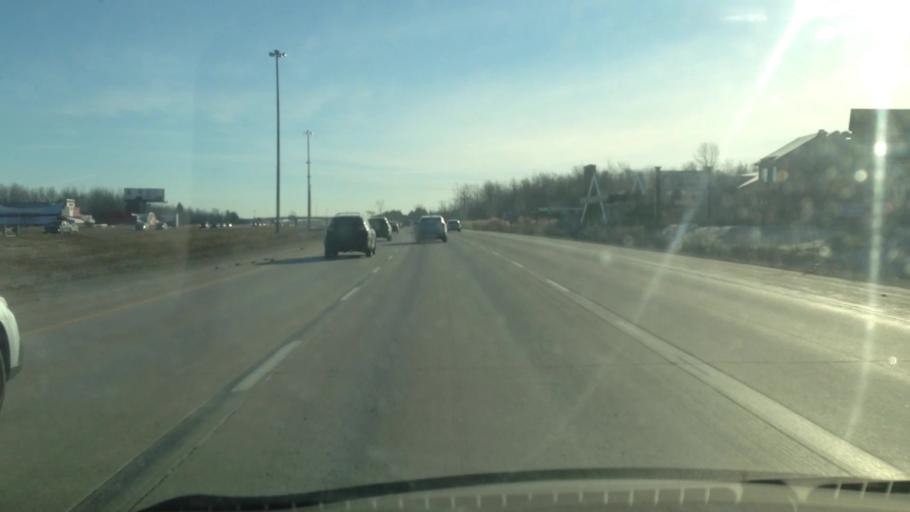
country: CA
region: Quebec
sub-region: Laurentides
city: Saint-Jerome
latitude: 45.7409
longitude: -73.9968
